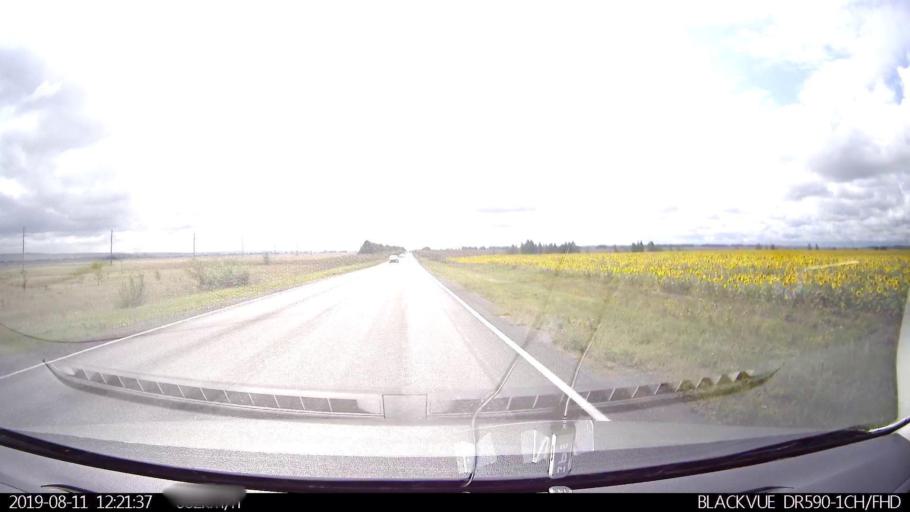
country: RU
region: Ulyanovsk
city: Ignatovka
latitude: 53.9190
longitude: 47.9573
